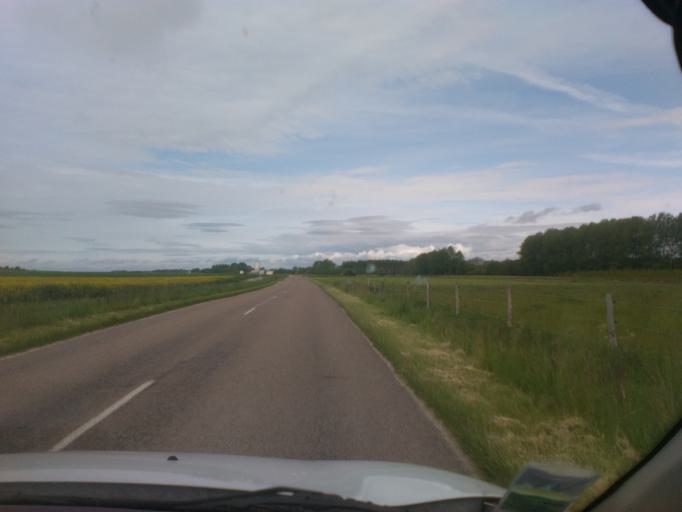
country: FR
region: Champagne-Ardenne
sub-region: Departement de l'Aube
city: Marigny-le-Chatel
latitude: 48.3559
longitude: 3.6915
